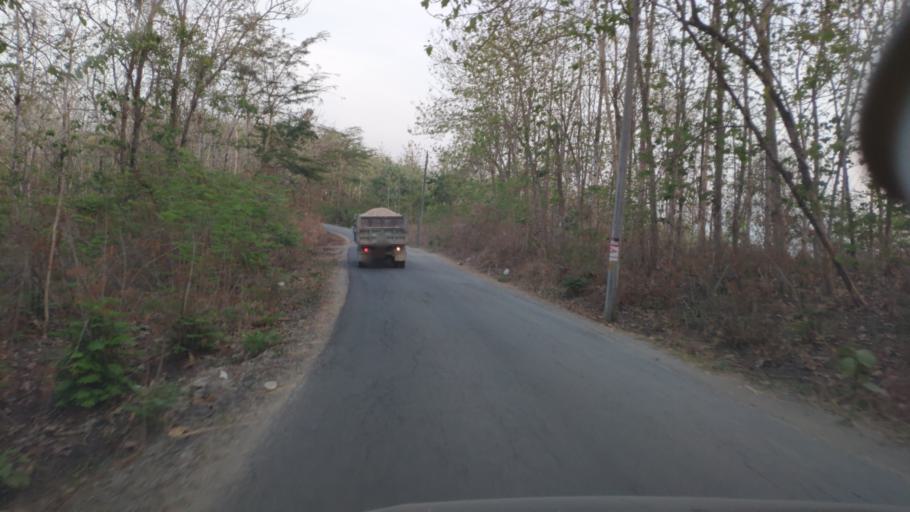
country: ID
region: Central Java
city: Semanggi
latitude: -7.0738
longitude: 111.4144
